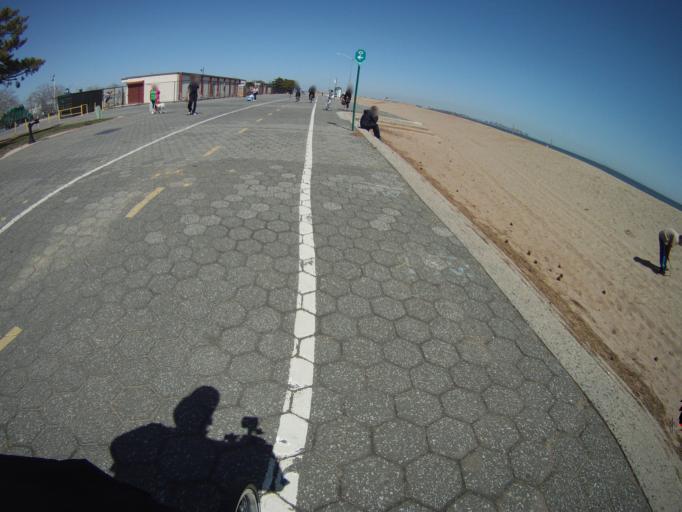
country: US
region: New York
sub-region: Richmond County
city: Staten Island
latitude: 40.5732
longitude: -74.0844
